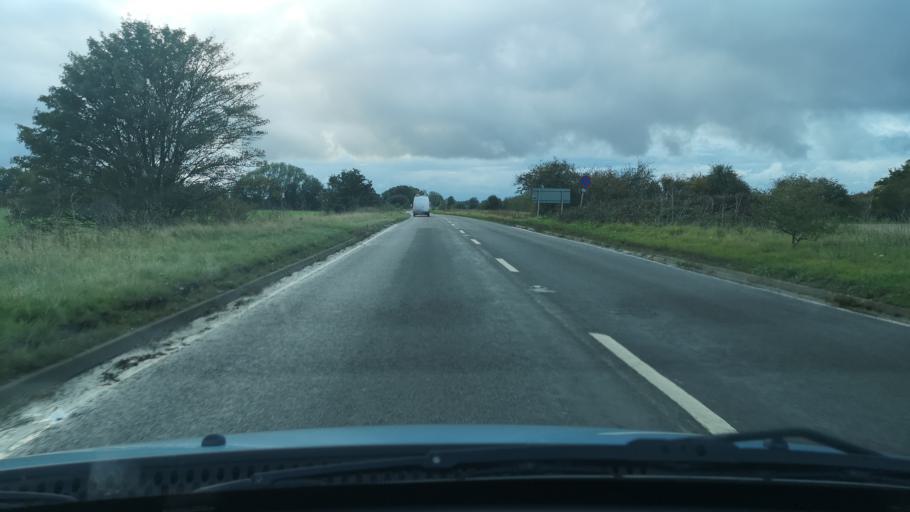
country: GB
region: England
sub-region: North Lincolnshire
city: Crowle
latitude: 53.5821
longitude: -0.8922
